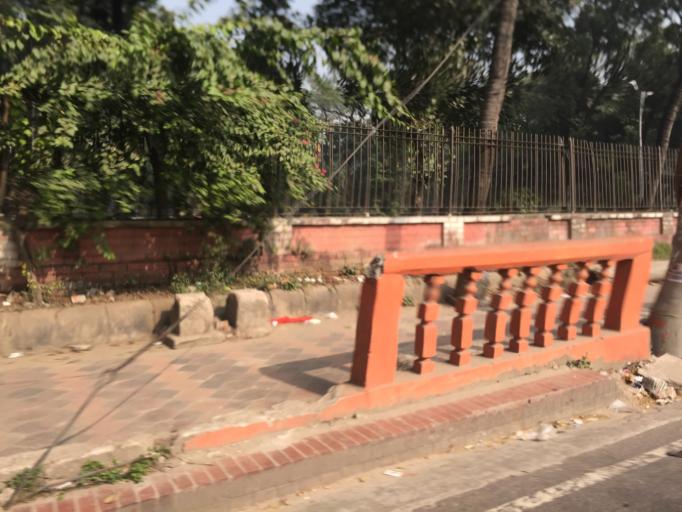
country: BD
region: Dhaka
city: Paltan
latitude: 23.7343
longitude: 90.4015
